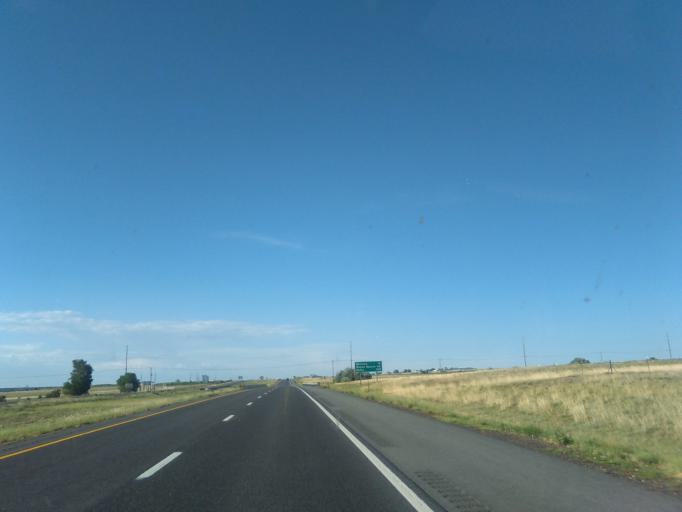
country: US
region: New Mexico
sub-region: San Miguel County
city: Las Vegas
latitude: 35.6380
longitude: -105.1980
